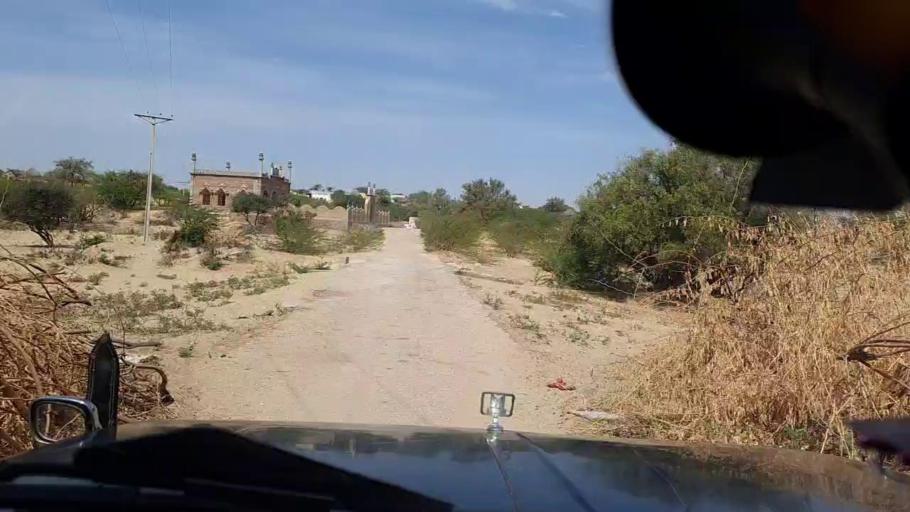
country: PK
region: Sindh
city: Diplo
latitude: 24.4403
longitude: 69.5374
